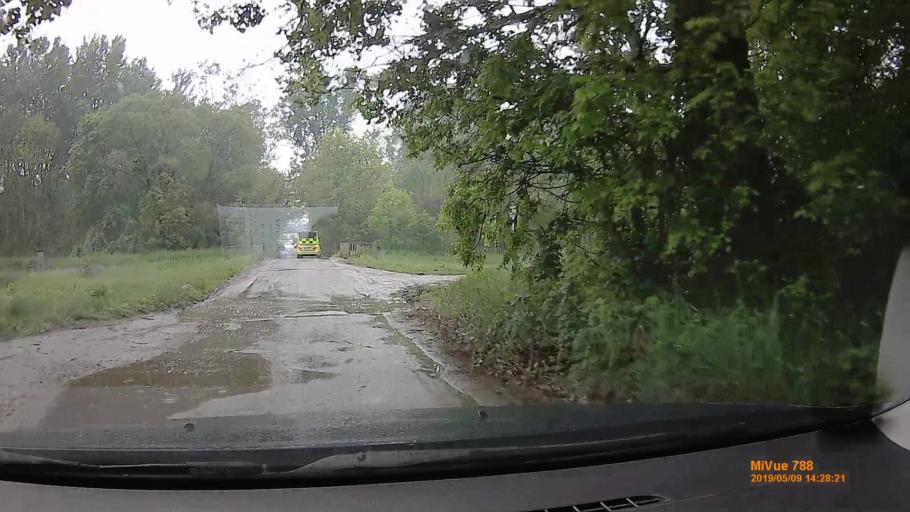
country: HU
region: Budapest
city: Budapest XVII. keruelet
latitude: 47.4902
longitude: 19.2204
